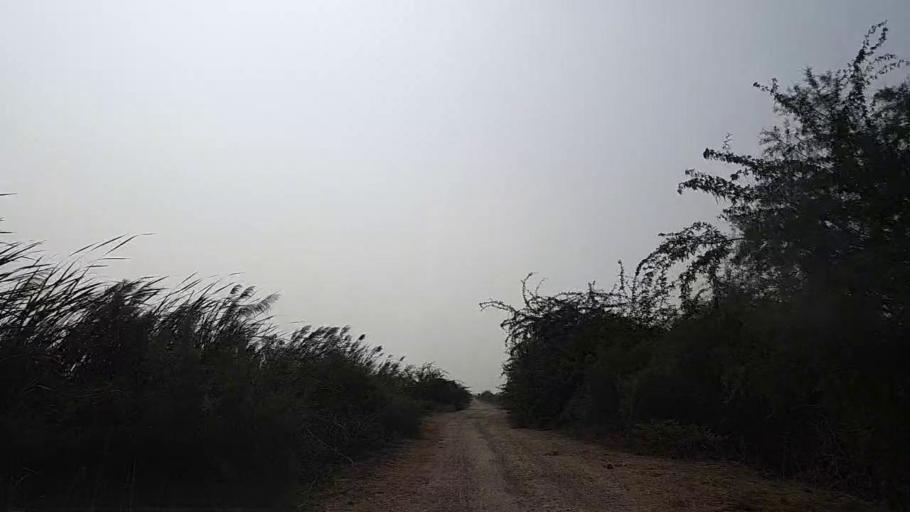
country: PK
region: Sindh
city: Thatta
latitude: 24.6968
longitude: 67.8009
